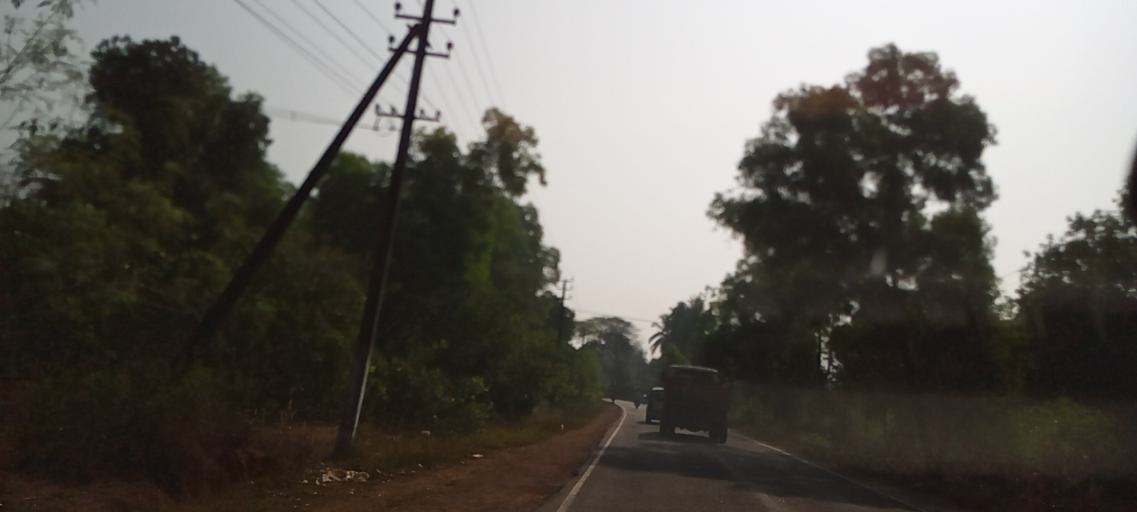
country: IN
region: Karnataka
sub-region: Udupi
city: Coondapoor
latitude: 13.5155
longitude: 74.7516
